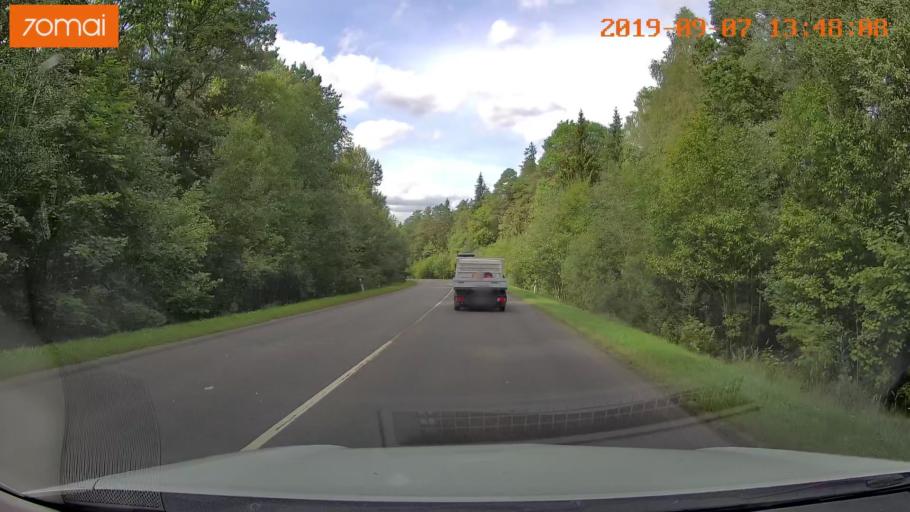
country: LT
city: Baltoji Voke
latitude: 54.6011
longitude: 25.2061
